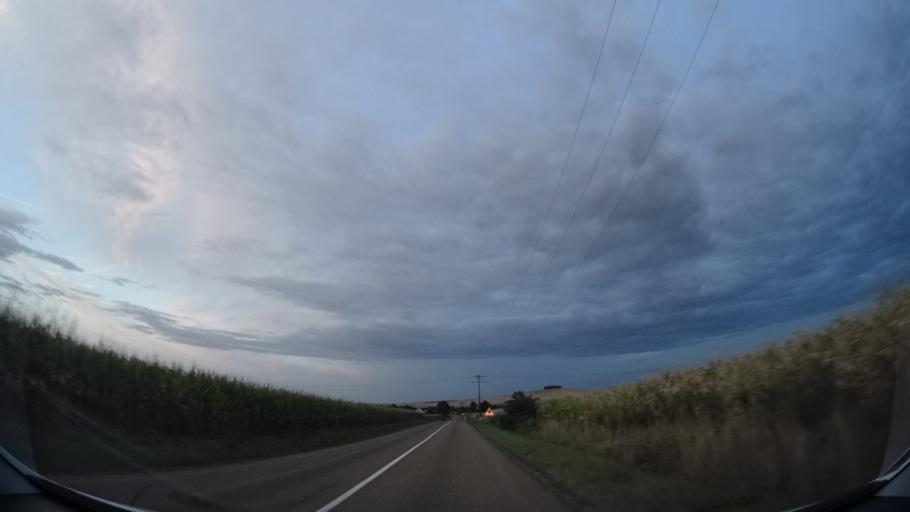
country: FR
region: Bourgogne
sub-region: Departement de l'Yonne
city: Aillant-sur-Tholon
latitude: 47.9147
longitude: 3.3445
